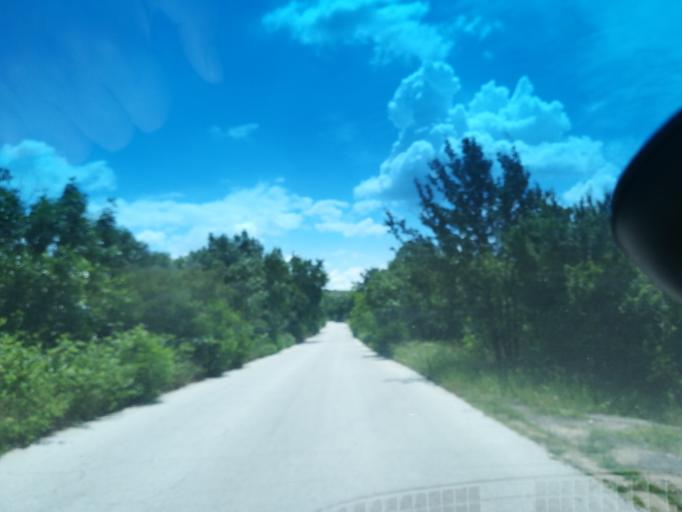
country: BG
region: Khaskovo
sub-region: Obshtina Mineralni Bani
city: Mineralni Bani
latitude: 41.9892
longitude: 25.2411
